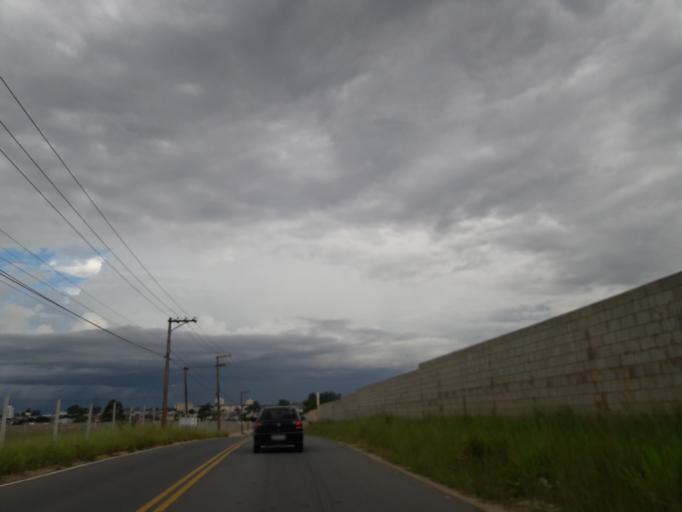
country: BR
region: Sao Paulo
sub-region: Aruja
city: Aruja
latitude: -23.3942
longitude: -46.4091
